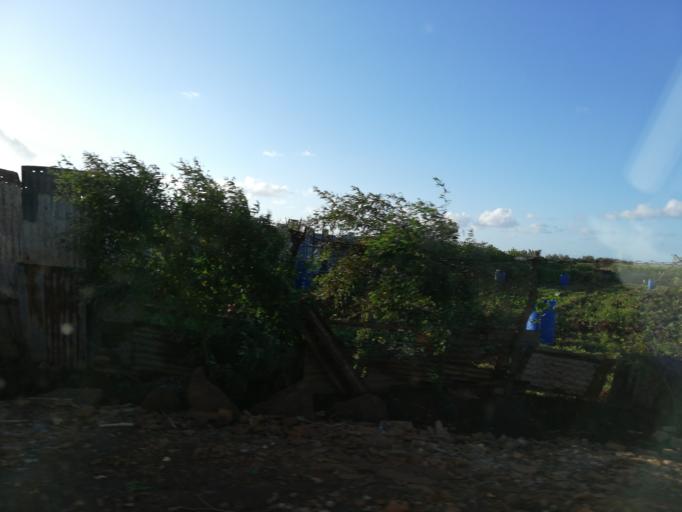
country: MU
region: Pamplemousses
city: Morcellemont Saint Andre
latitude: -20.0800
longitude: 57.5354
